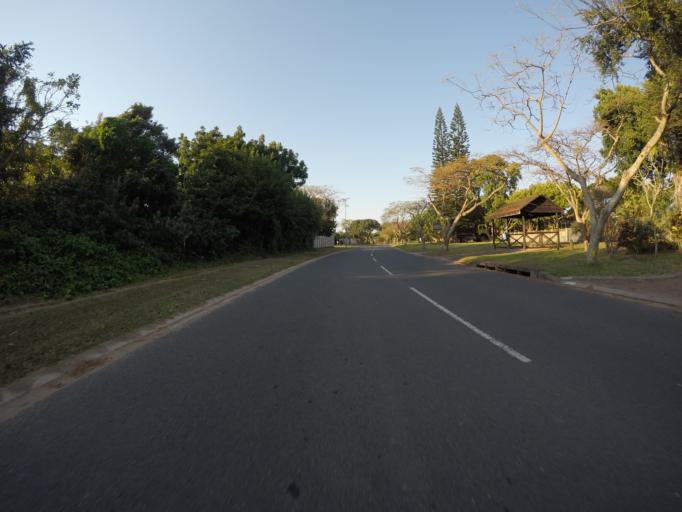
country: ZA
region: KwaZulu-Natal
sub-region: uThungulu District Municipality
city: Richards Bay
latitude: -28.7793
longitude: 32.1109
